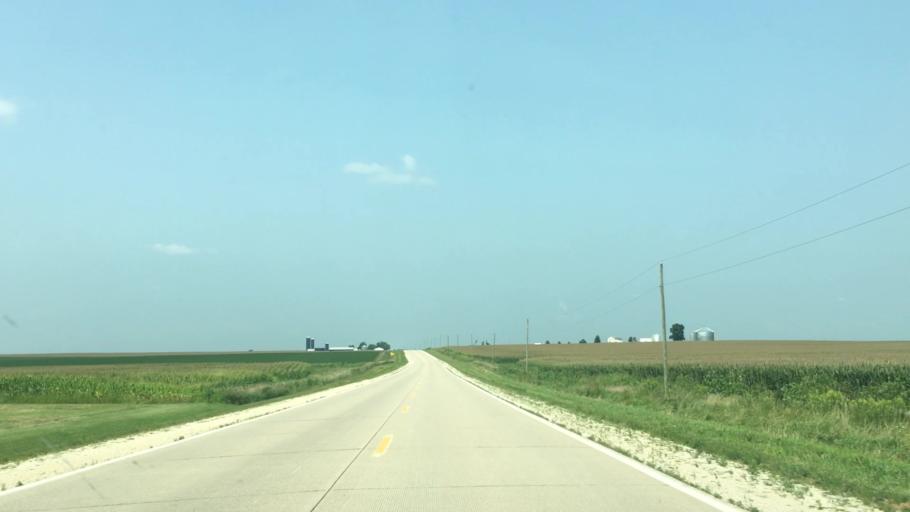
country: US
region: Iowa
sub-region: Fayette County
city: Fayette
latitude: 42.7286
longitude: -91.8041
